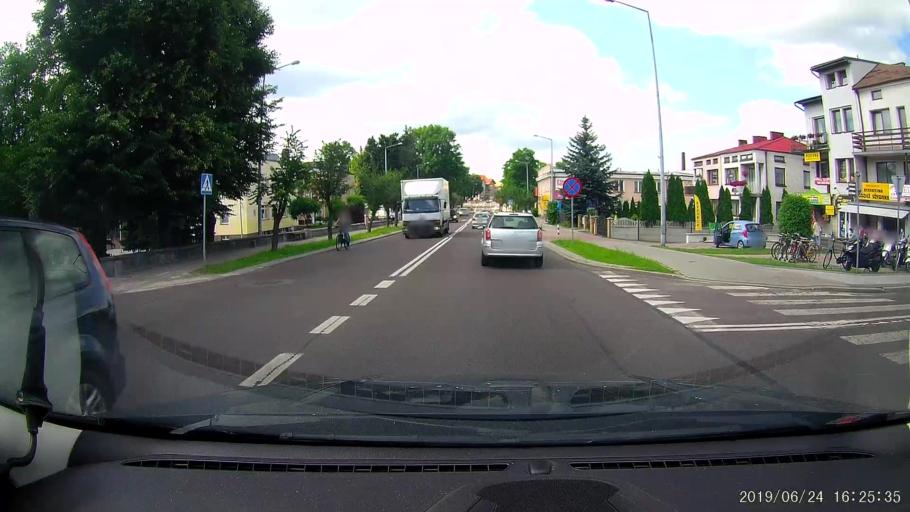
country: PL
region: Lublin Voivodeship
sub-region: Powiat tomaszowski
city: Tomaszow Lubelski
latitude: 50.4447
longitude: 23.4170
